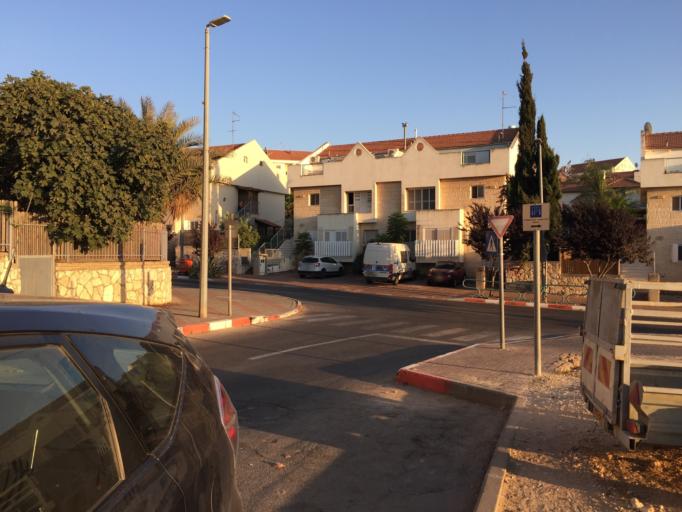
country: PS
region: West Bank
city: Marda
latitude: 32.1036
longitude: 35.1955
